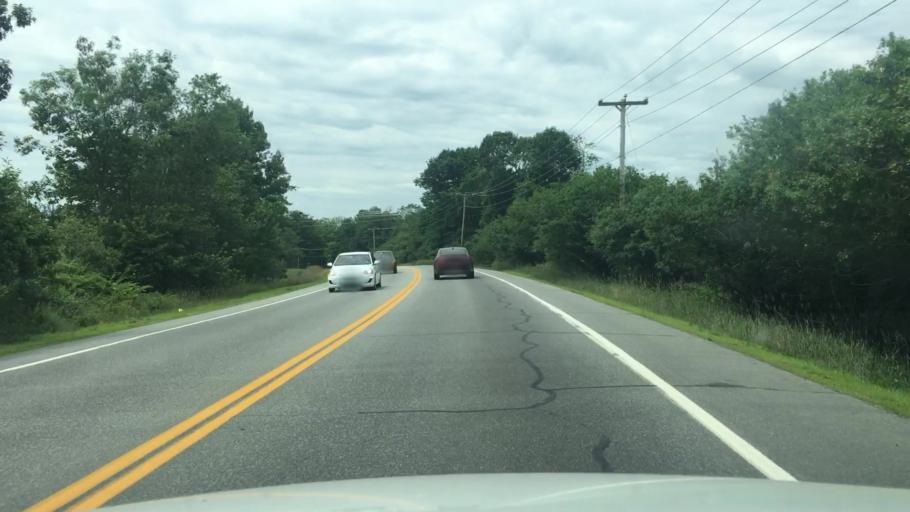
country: US
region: Maine
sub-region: Waldo County
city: Palermo
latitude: 44.4103
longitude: -69.5257
